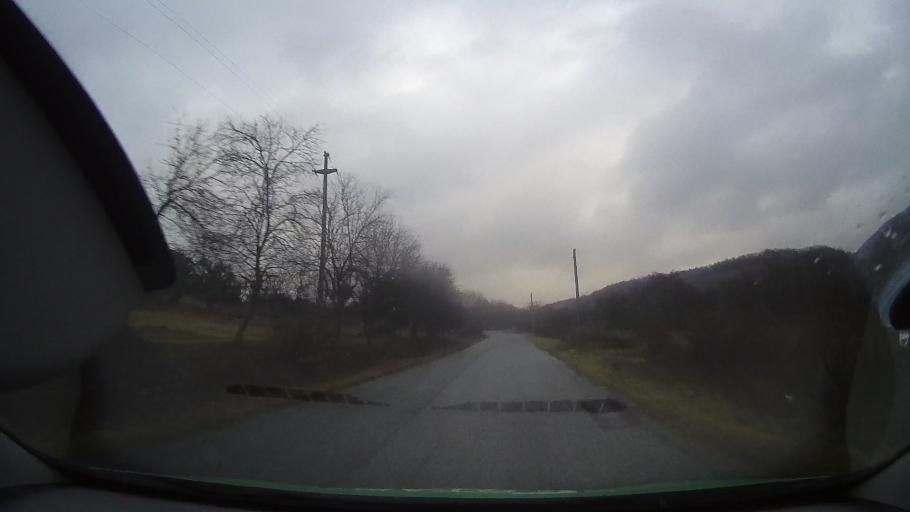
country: RO
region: Hunedoara
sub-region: Comuna Ribita
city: Ribita
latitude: 46.2305
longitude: 22.7367
